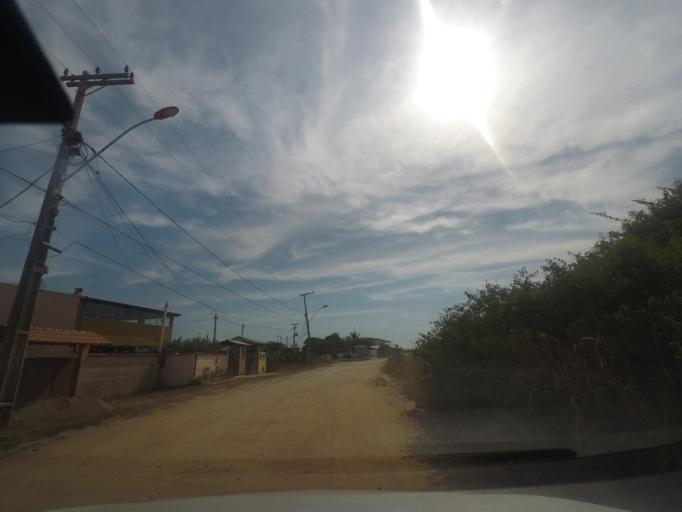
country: BR
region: Rio de Janeiro
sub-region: Marica
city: Marica
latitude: -22.9596
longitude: -42.8359
